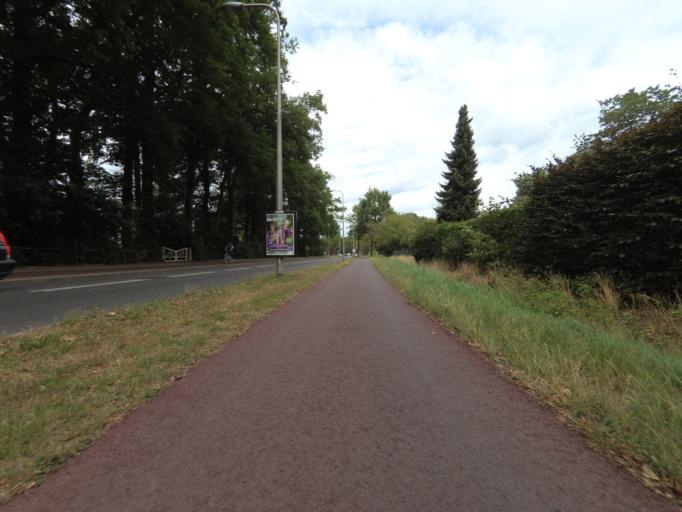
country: NL
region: Overijssel
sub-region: Gemeente Enschede
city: Enschede
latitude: 52.2242
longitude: 6.9289
